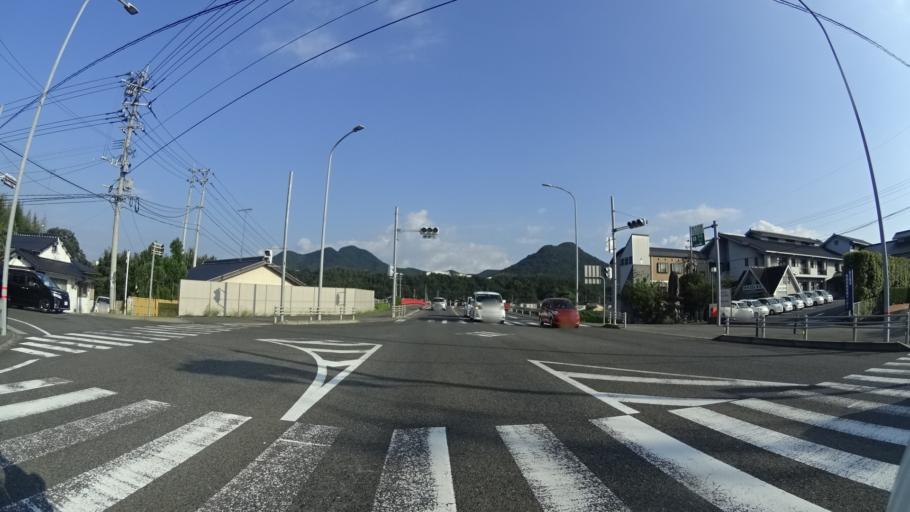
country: JP
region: Oita
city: Bungo-Takada-shi
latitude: 33.5089
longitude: 131.3277
